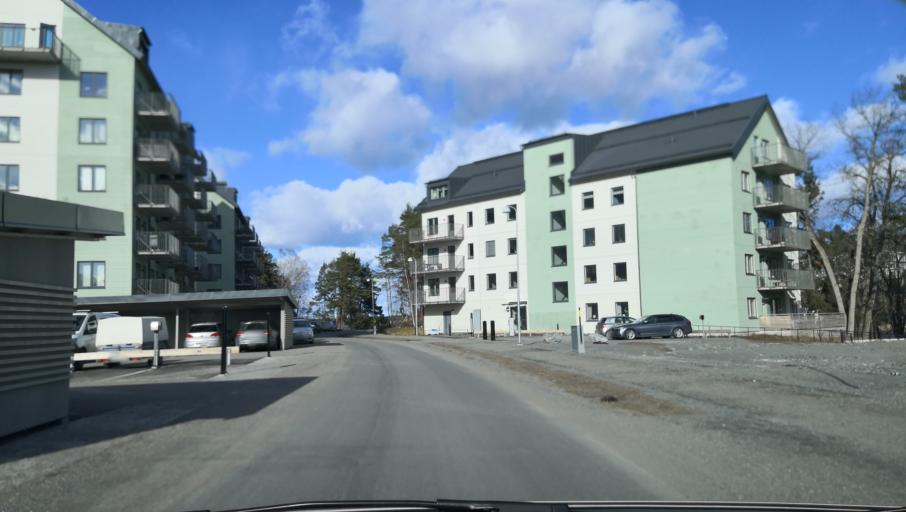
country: SE
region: Stockholm
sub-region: Varmdo Kommun
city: Mortnas
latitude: 59.3142
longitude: 18.4575
